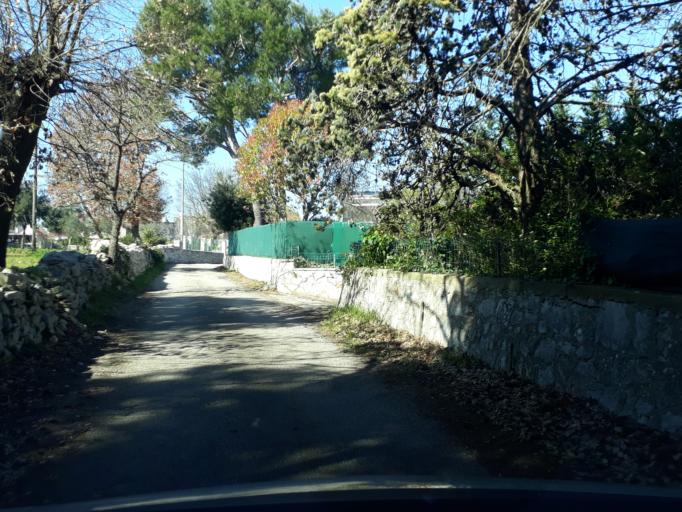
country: IT
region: Apulia
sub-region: Provincia di Brindisi
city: Lamie di Olimpie-Selva
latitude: 40.7975
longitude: 17.3473
